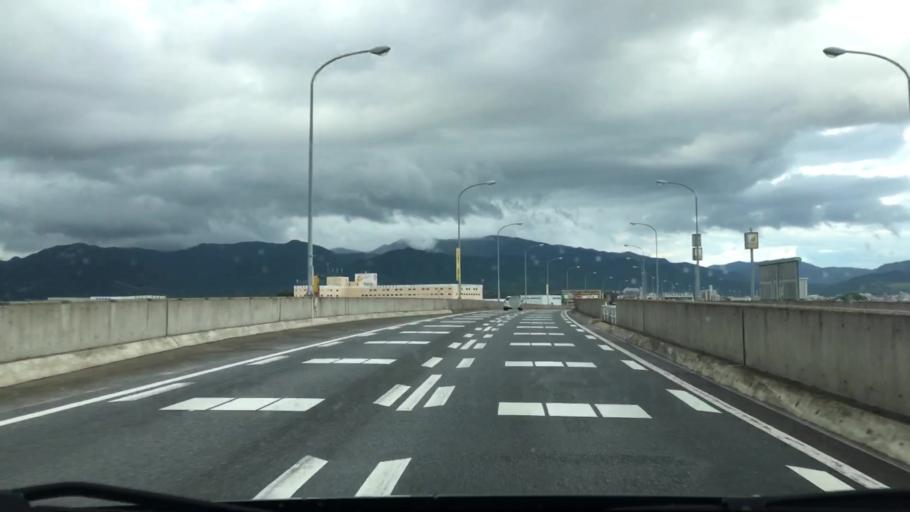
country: JP
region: Fukuoka
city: Fukuoka-shi
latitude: 33.6297
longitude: 130.4778
